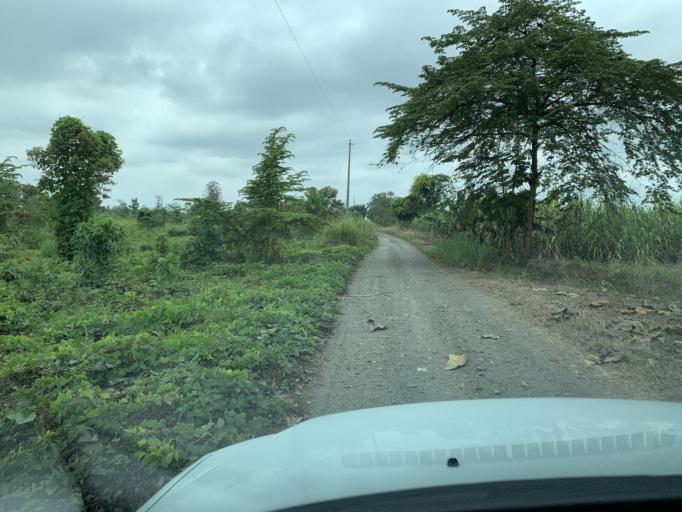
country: EC
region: Guayas
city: Coronel Marcelino Mariduena
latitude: -2.3450
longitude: -79.4588
